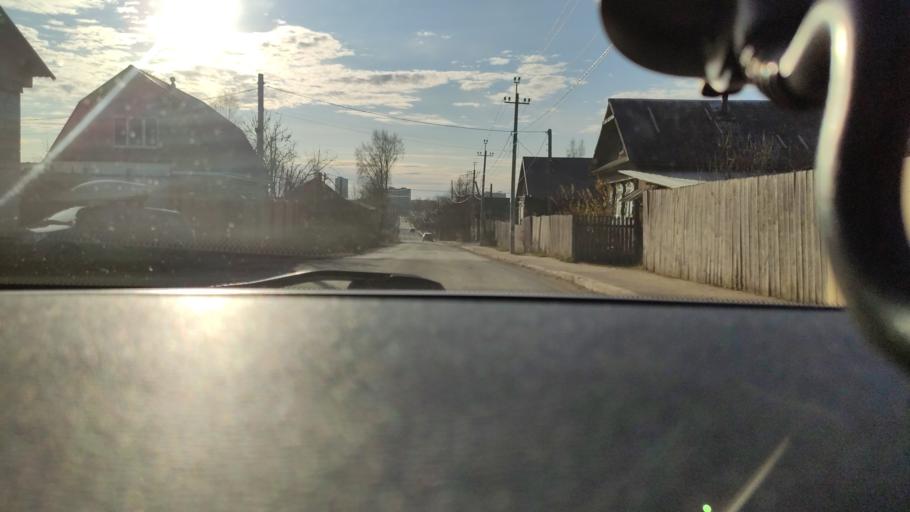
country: RU
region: Perm
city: Kondratovo
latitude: 58.0528
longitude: 56.0286
